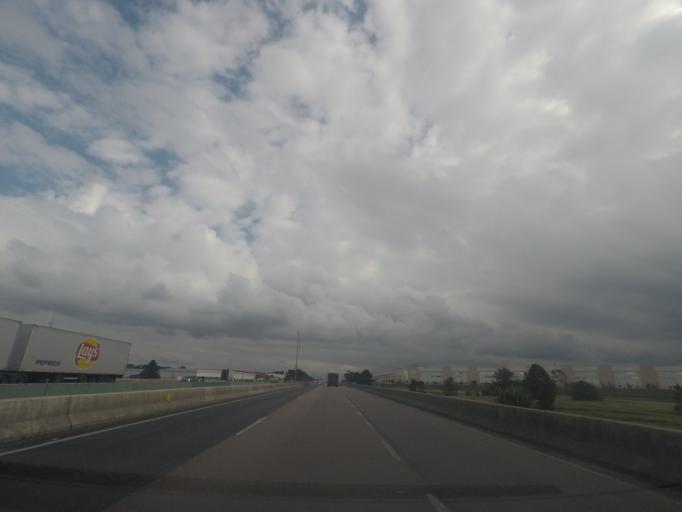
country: BR
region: Parana
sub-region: Sao Jose Dos Pinhais
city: Sao Jose dos Pinhais
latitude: -25.5112
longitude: -49.1279
